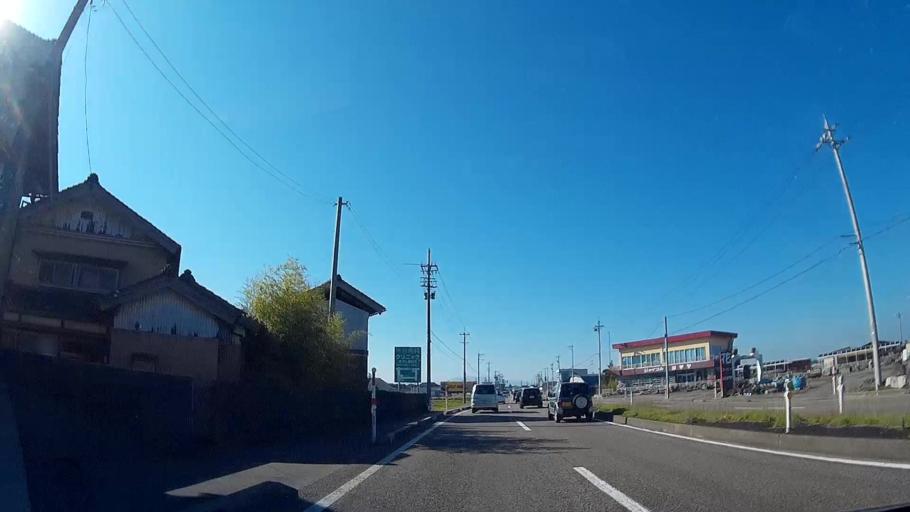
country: JP
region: Toyama
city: Takaoka
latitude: 36.6946
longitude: 136.9823
